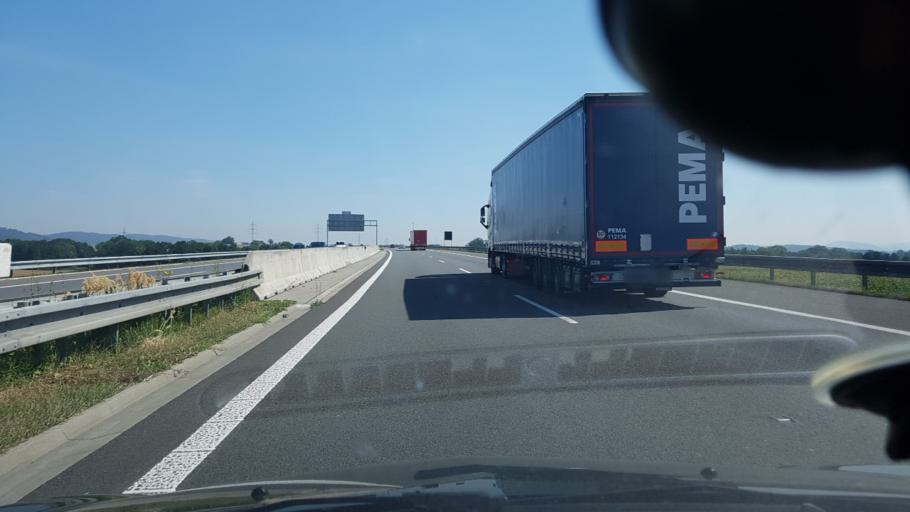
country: CZ
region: Olomoucky
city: Belotin
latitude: 49.5901
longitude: 17.7776
